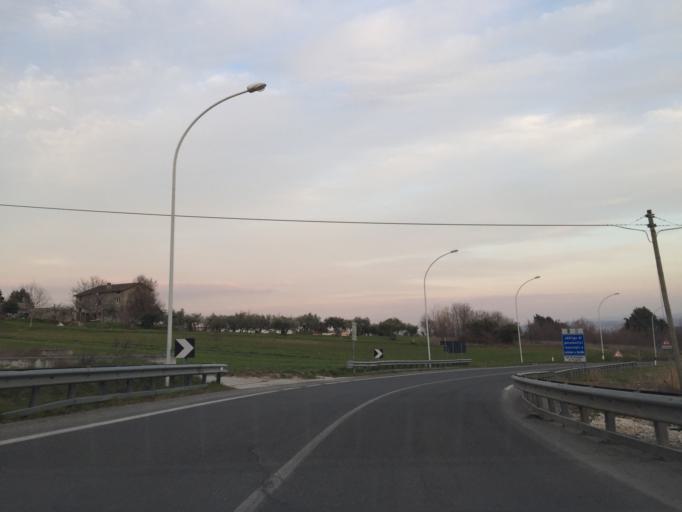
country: IT
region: Molise
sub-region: Provincia di Campobasso
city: Campobasso
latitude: 41.5626
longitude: 14.6843
